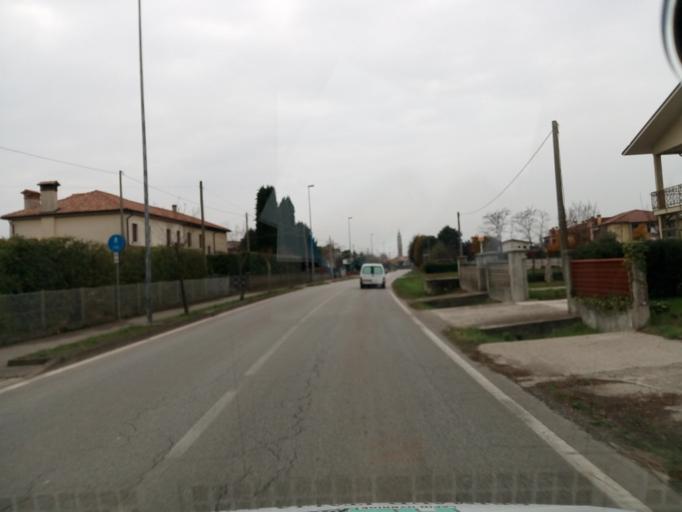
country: IT
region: Veneto
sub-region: Provincia di Treviso
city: Trevignano
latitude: 45.7392
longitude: 12.0750
